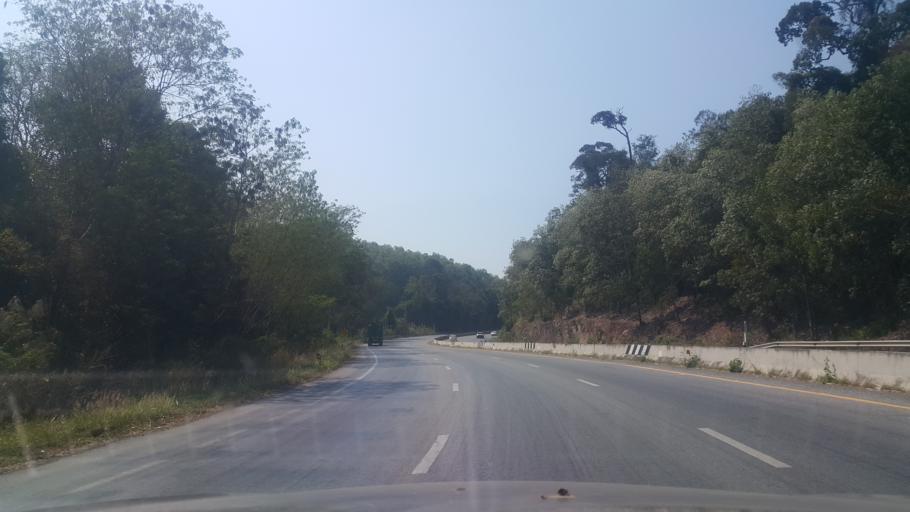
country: TH
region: Nakhon Ratchasima
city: Wang Nam Khiao
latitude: 14.4535
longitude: 101.8993
